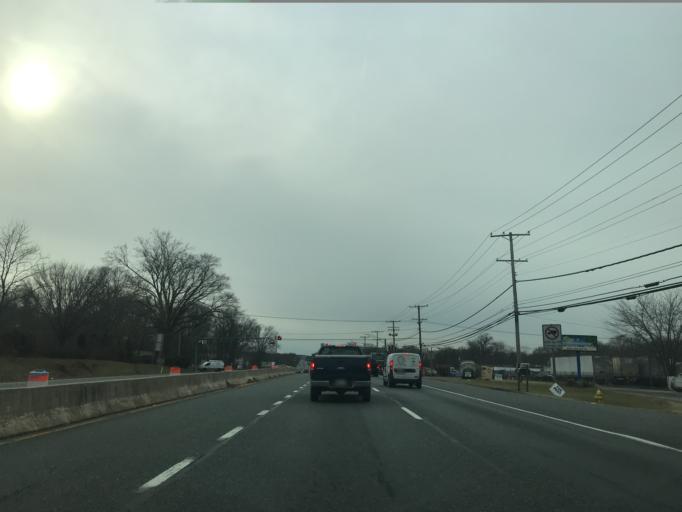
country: US
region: Maryland
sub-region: Harford County
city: Perryman
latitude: 39.4839
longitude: -76.2089
